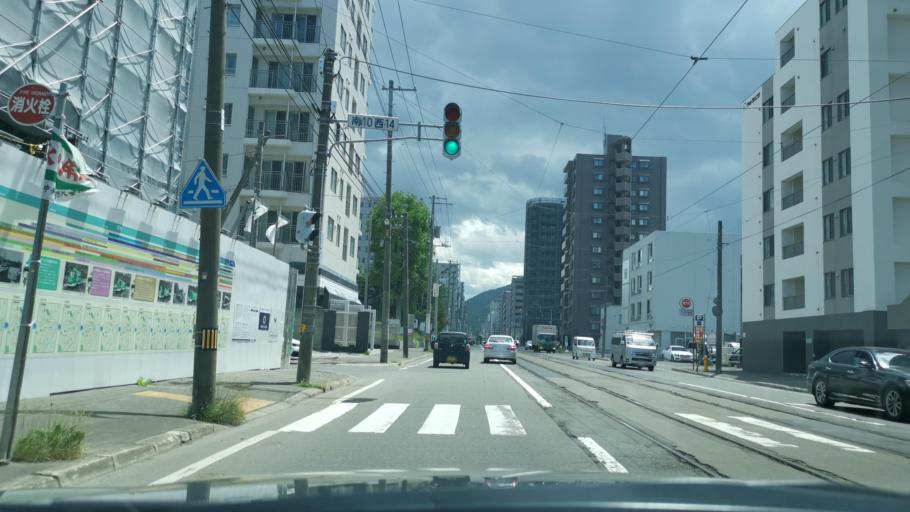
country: JP
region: Hokkaido
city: Sapporo
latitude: 43.0465
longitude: 141.3358
